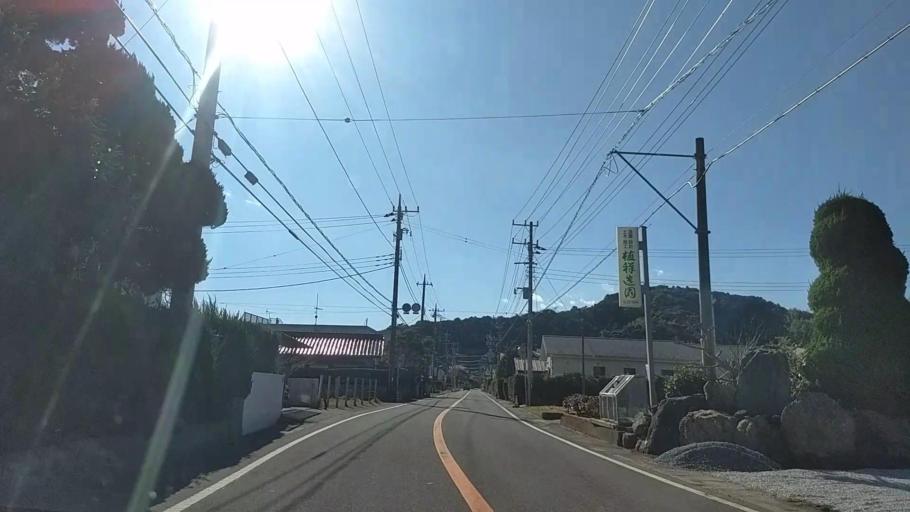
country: JP
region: Chiba
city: Tateyama
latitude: 34.9775
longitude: 139.8634
